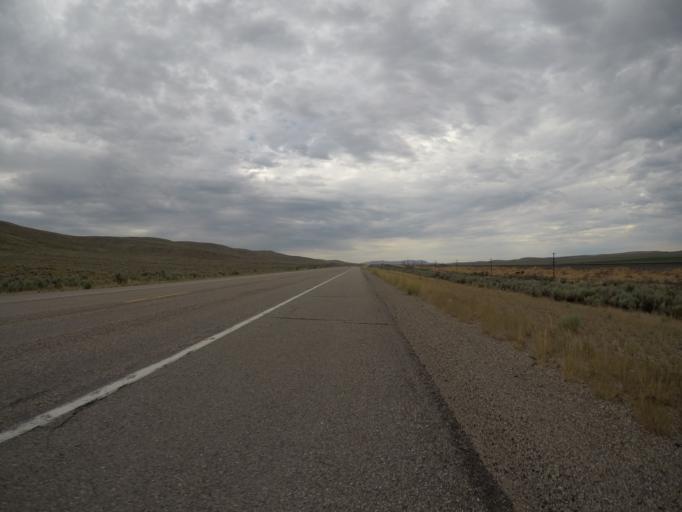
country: US
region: Utah
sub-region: Rich County
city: Randolph
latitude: 41.8449
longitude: -110.9748
